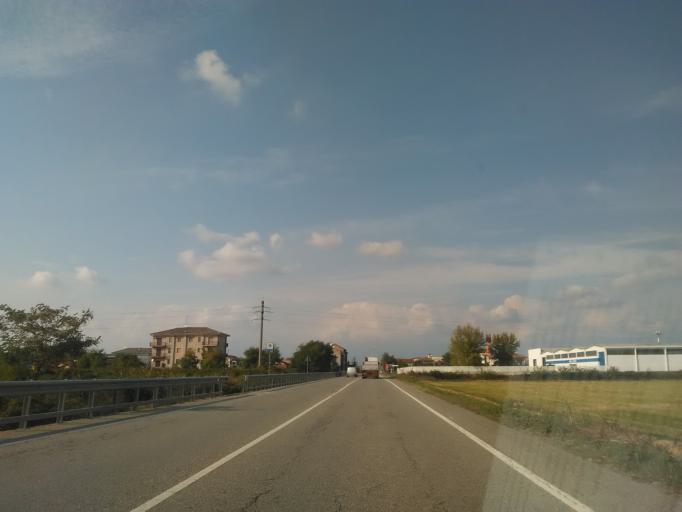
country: IT
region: Piedmont
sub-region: Provincia di Vercelli
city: Balocco
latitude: 45.4426
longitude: 8.2352
